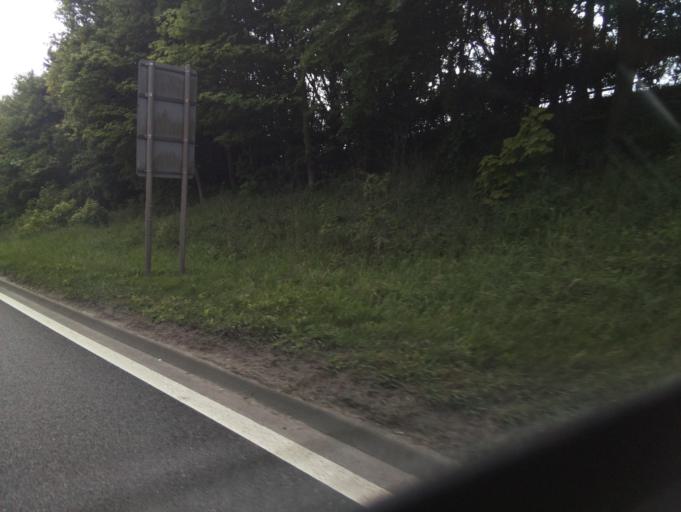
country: GB
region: England
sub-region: County Durham
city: Houghton-le-Spring
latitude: 54.8747
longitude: -1.4520
